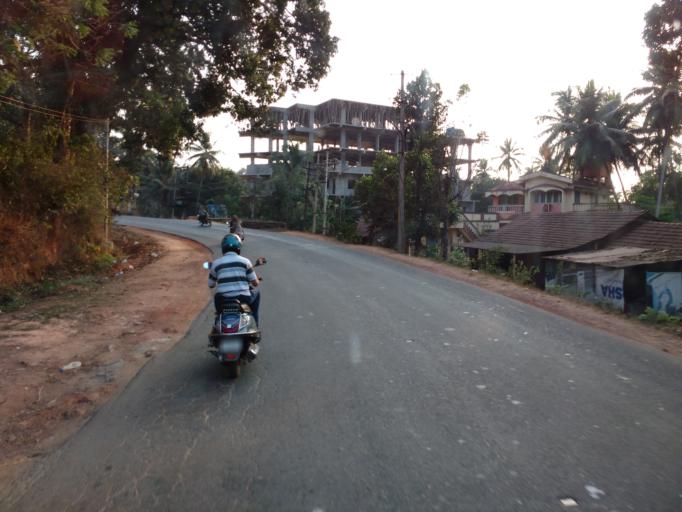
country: IN
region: Karnataka
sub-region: Dakshina Kannada
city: Mangalore
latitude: 12.8959
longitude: 74.8899
